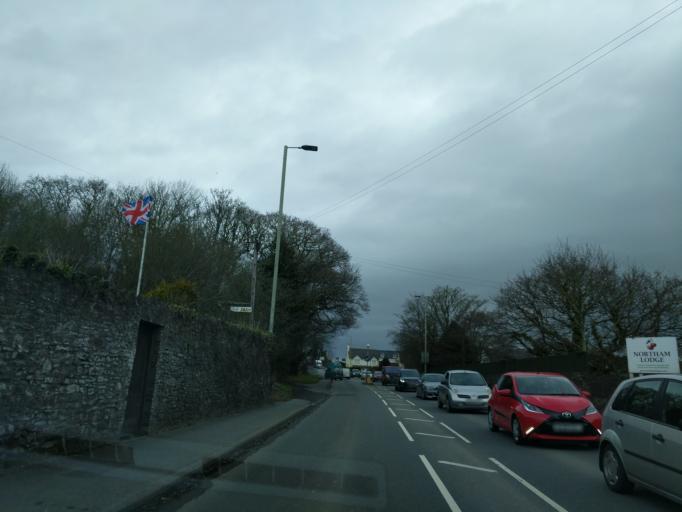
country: GB
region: England
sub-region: Devon
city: Northam
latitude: 51.0319
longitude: -4.2125
